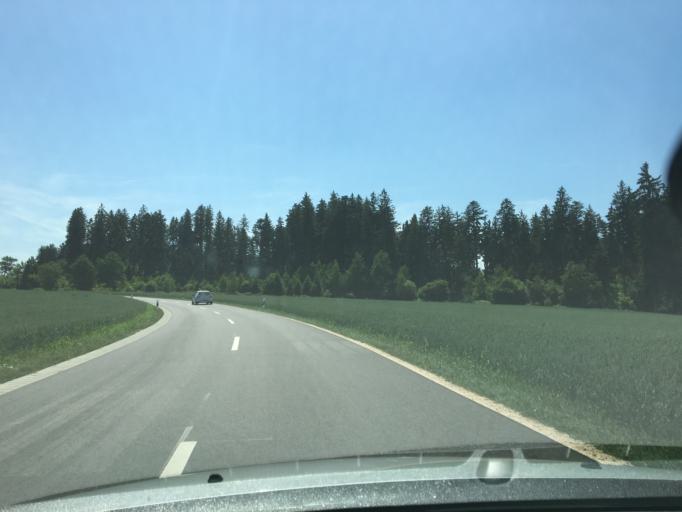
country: DE
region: Bavaria
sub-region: Upper Bavaria
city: Halsbach
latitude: 48.1152
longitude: 12.6796
